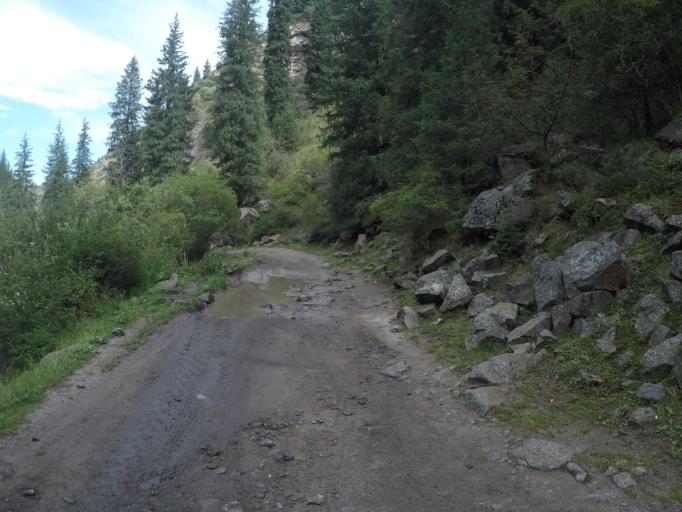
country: KG
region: Ysyk-Koel
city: Teploklyuchenka
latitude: 42.4379
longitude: 78.5600
